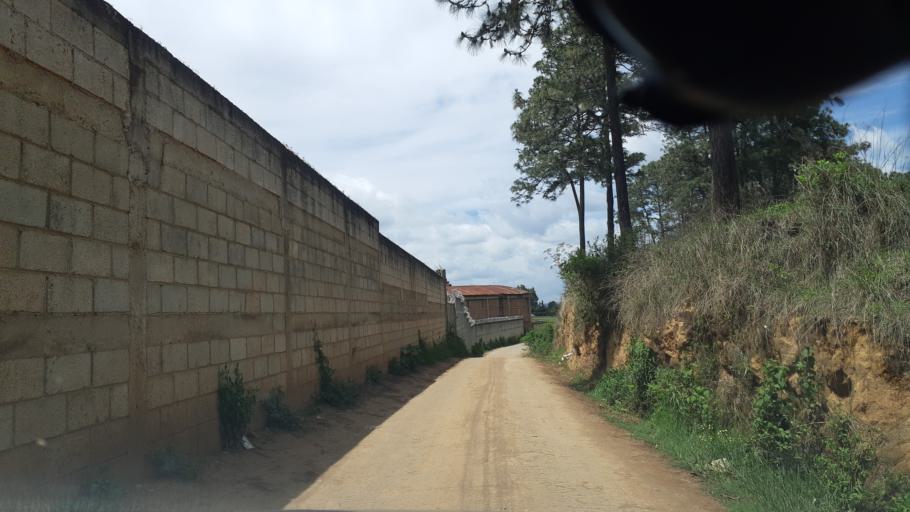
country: GT
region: Chimaltenango
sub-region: Municipio de Chimaltenango
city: Chimaltenango
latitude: 14.6561
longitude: -90.8402
